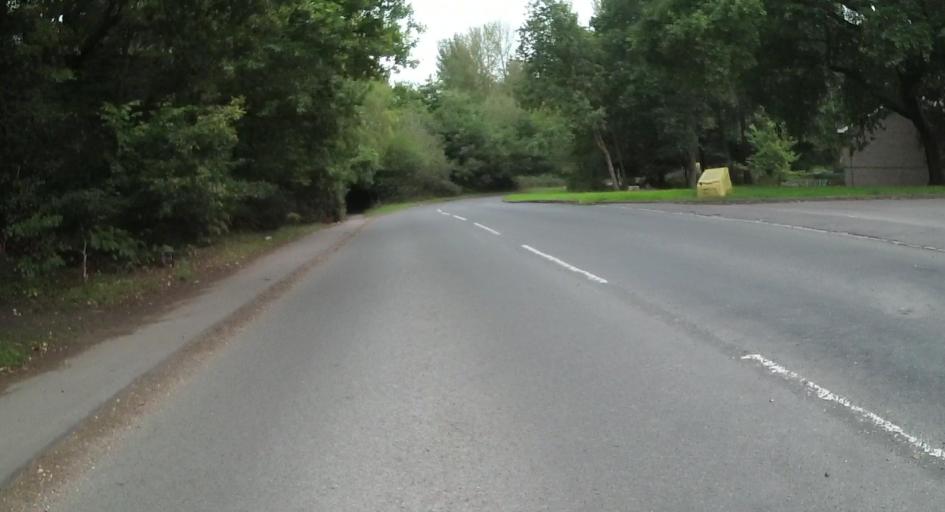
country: GB
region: England
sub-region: Surrey
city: Pirbright
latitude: 51.3056
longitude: -0.6508
